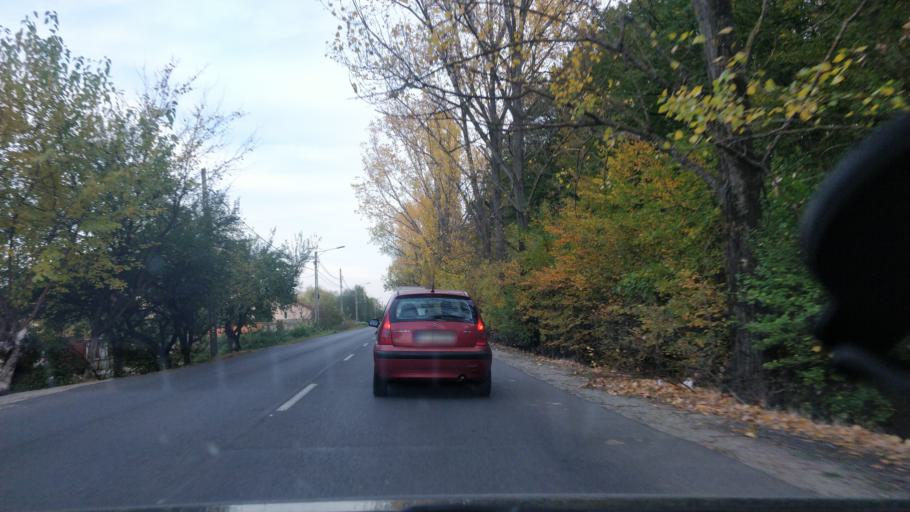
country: RO
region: Ilfov
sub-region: Comuna Ciorogarla
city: Ciorogarla
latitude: 44.4468
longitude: 25.8539
